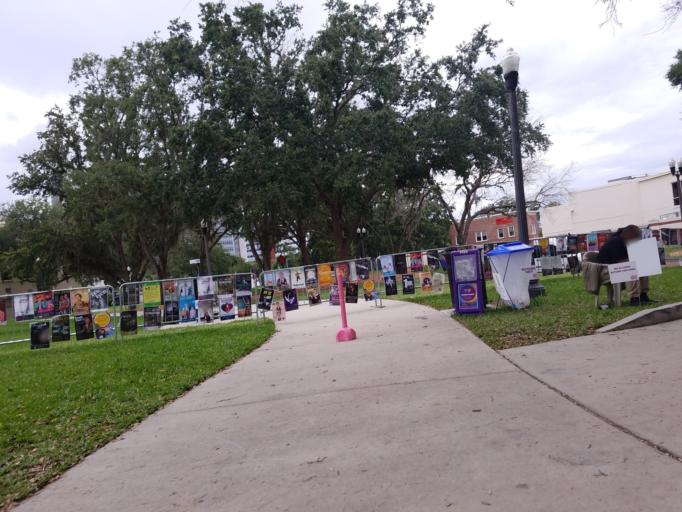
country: US
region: Florida
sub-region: Orange County
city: Fairview Shores
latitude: 28.5721
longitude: -81.3670
